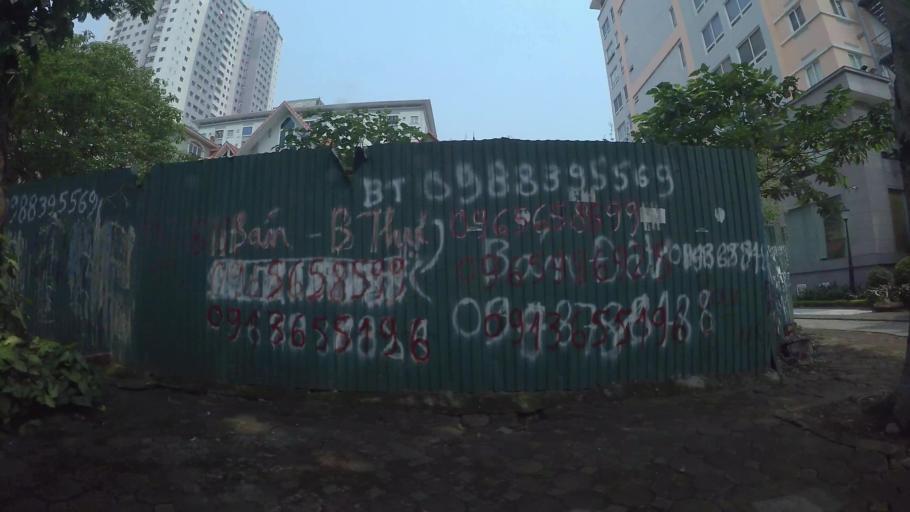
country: VN
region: Ha Noi
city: Van Dien
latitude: 20.9625
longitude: 105.8329
